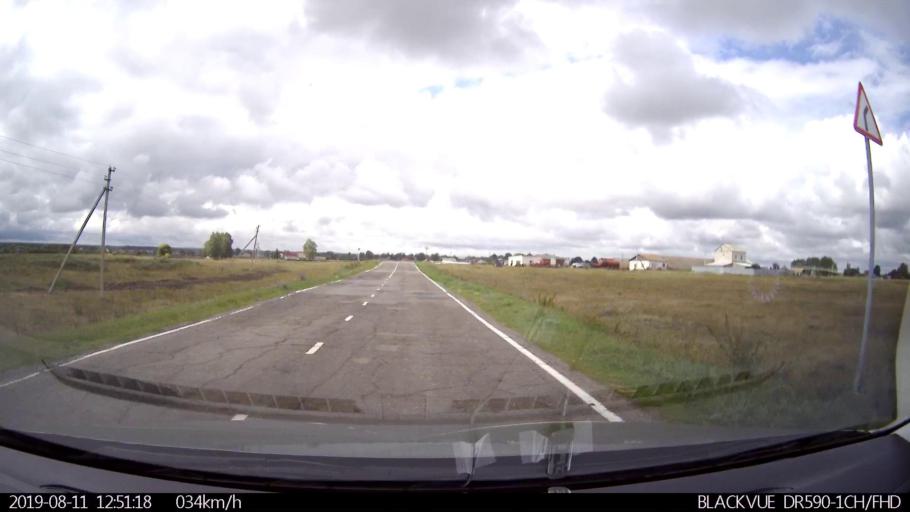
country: RU
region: Ulyanovsk
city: Ignatovka
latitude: 53.8756
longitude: 47.6638
